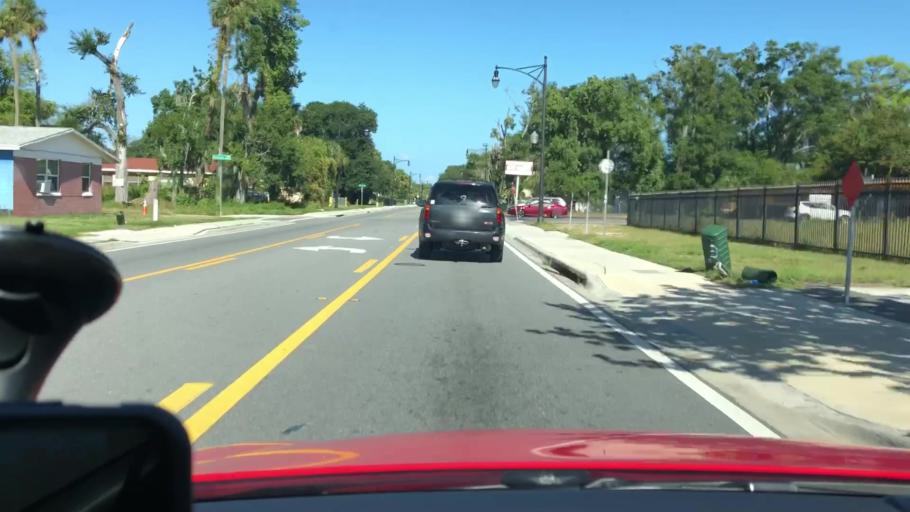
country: US
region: Florida
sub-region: Volusia County
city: Daytona Beach
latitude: 29.2035
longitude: -81.0294
